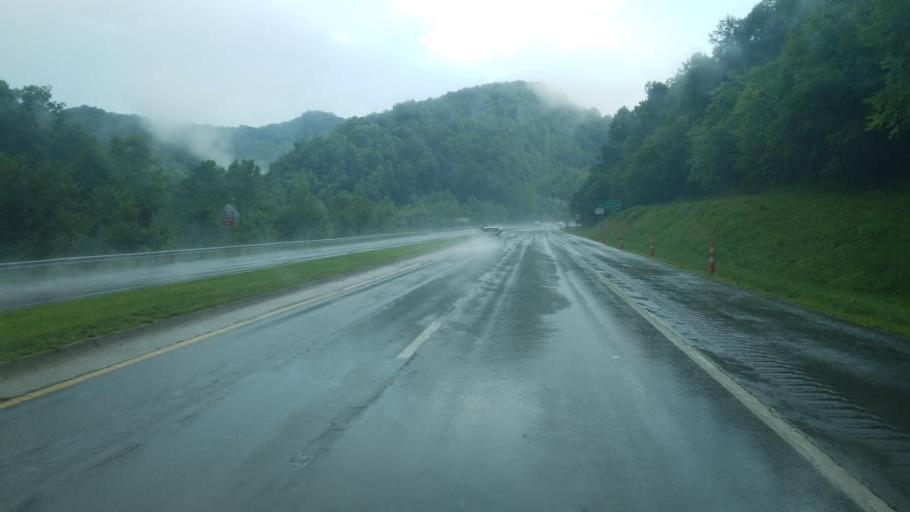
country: US
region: West Virginia
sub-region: Logan County
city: Chapmanville
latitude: 37.9760
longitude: -81.9964
